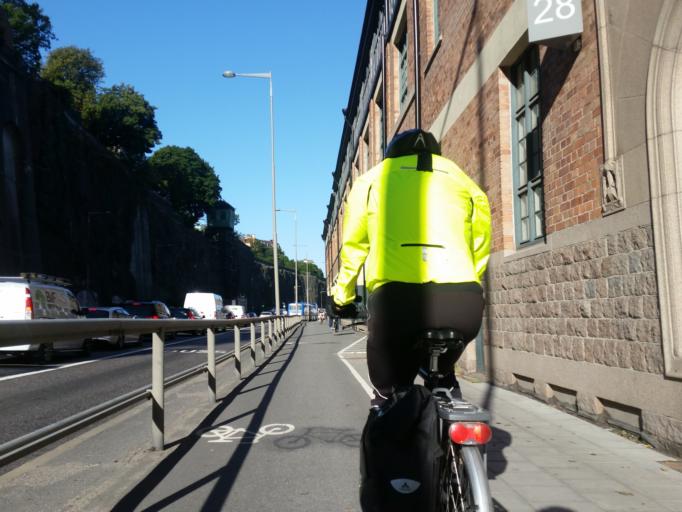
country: SE
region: Stockholm
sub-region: Stockholms Kommun
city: OEstermalm
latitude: 59.3177
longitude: 18.0867
